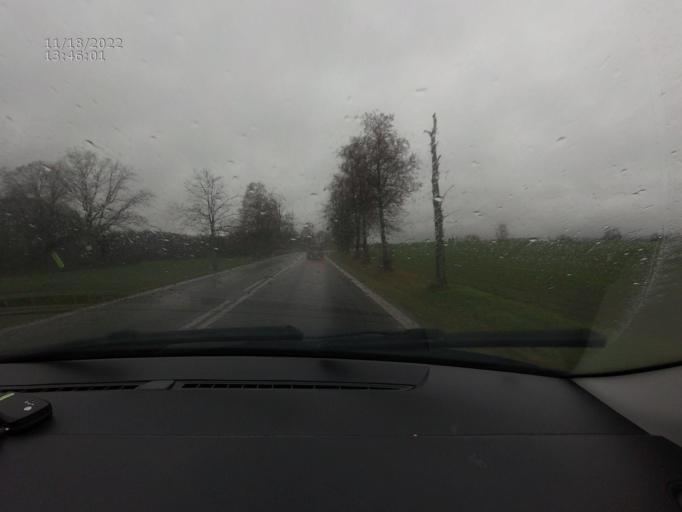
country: CZ
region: Jihocesky
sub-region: Okres Strakonice
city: Blatna
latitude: 49.4264
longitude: 13.8584
